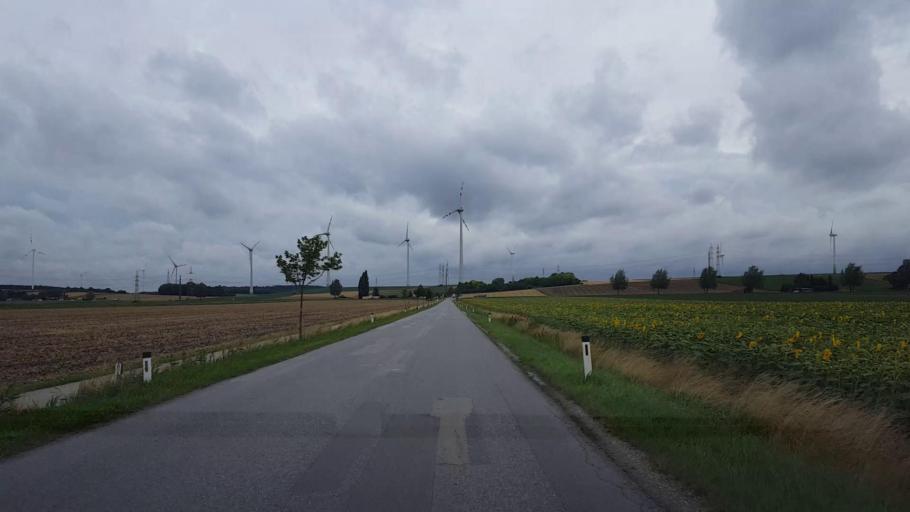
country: AT
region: Lower Austria
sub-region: Politischer Bezirk Bruck an der Leitha
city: Bruck an der Leitha
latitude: 48.0239
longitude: 16.7197
